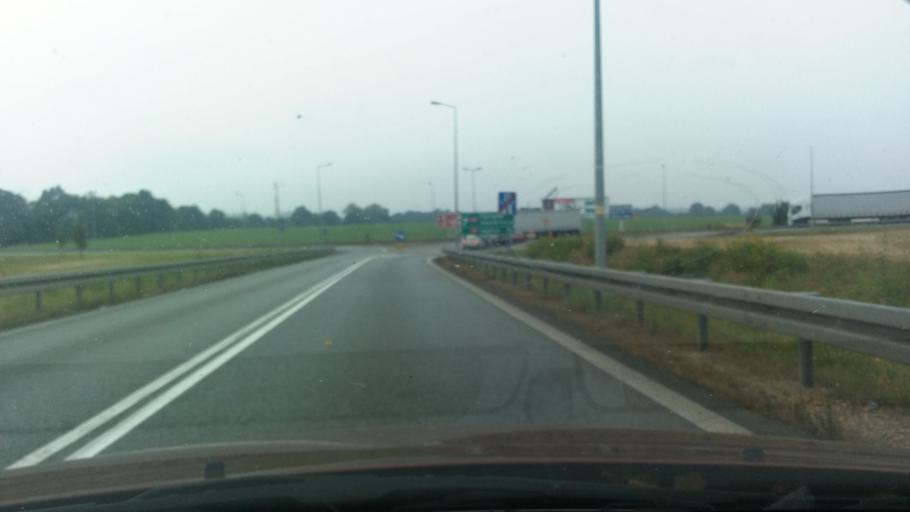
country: PL
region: Lower Silesian Voivodeship
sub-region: Powiat zgorzelecki
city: Lagow
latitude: 51.1702
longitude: 15.0317
